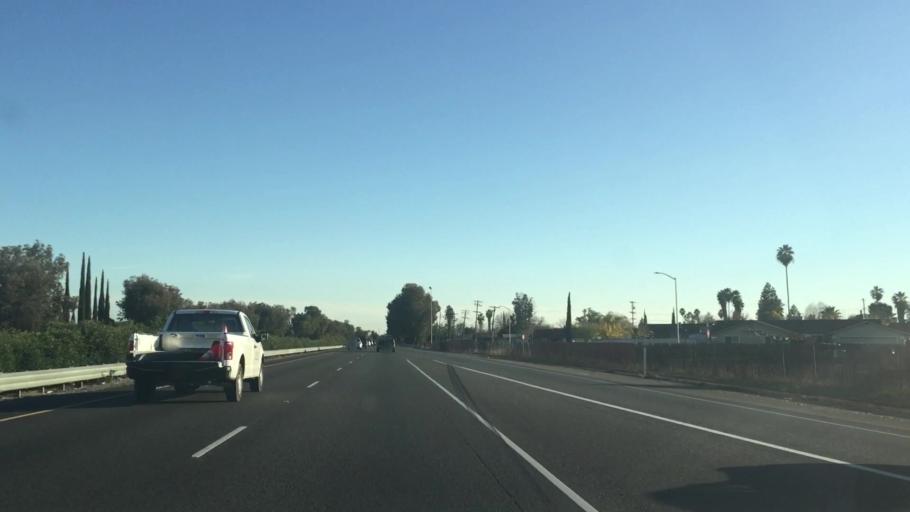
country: US
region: California
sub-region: Yuba County
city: Olivehurst
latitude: 39.1113
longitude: -121.5579
